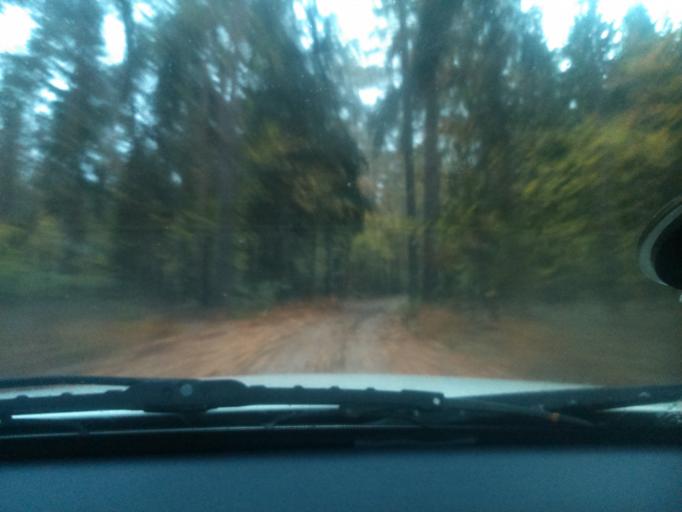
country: PL
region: Kujawsko-Pomorskie
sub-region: Powiat golubsko-dobrzynski
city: Radomin
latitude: 53.1382
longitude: 19.1313
